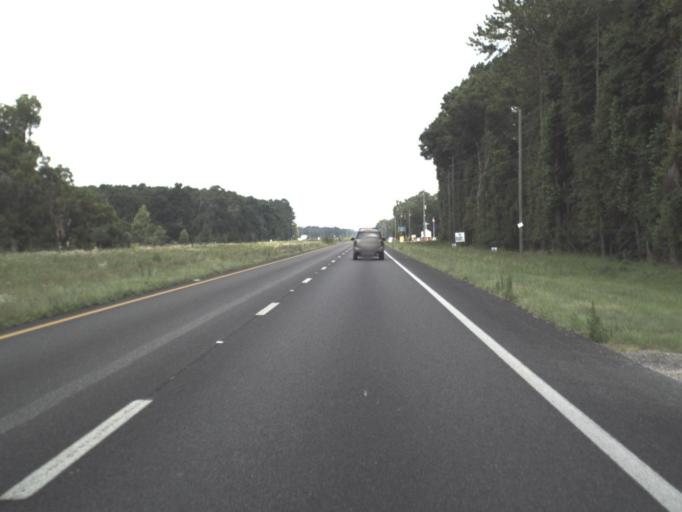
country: US
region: Florida
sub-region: Levy County
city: Williston
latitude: 29.3937
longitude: -82.4818
